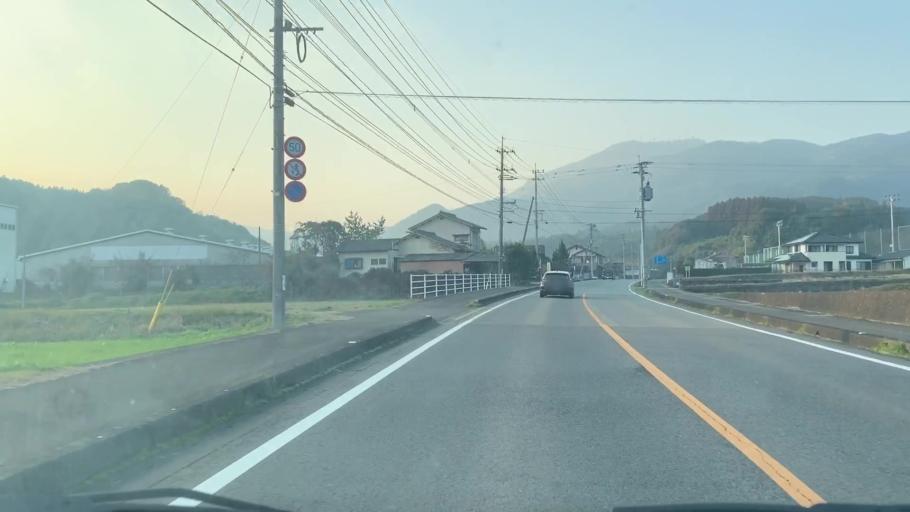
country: JP
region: Saga Prefecture
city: Takeocho-takeo
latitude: 33.2611
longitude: 130.0598
